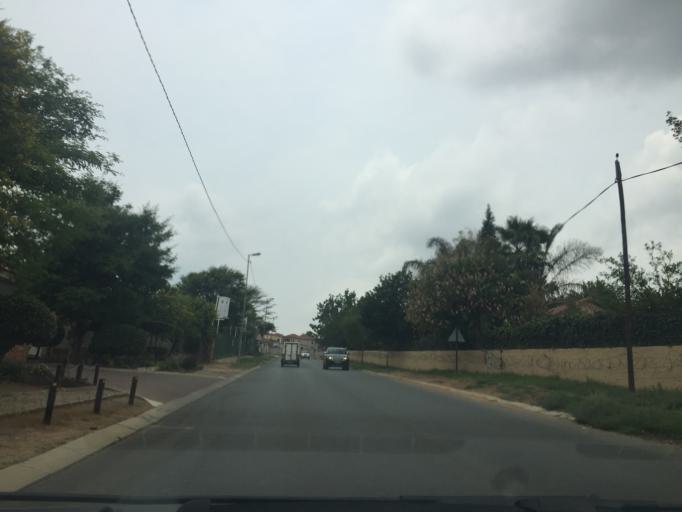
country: ZA
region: Gauteng
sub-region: City of Johannesburg Metropolitan Municipality
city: Diepsloot
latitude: -26.0177
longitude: 27.9964
